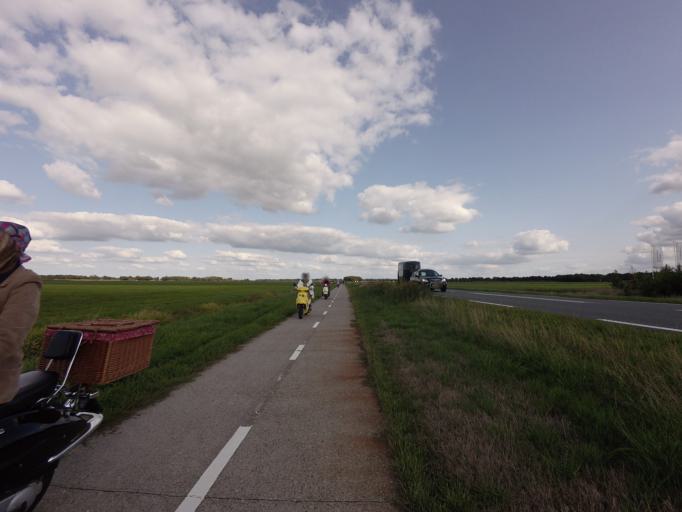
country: NL
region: Drenthe
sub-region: Gemeente Westerveld
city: Dwingeloo
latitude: 52.8393
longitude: 6.3831
